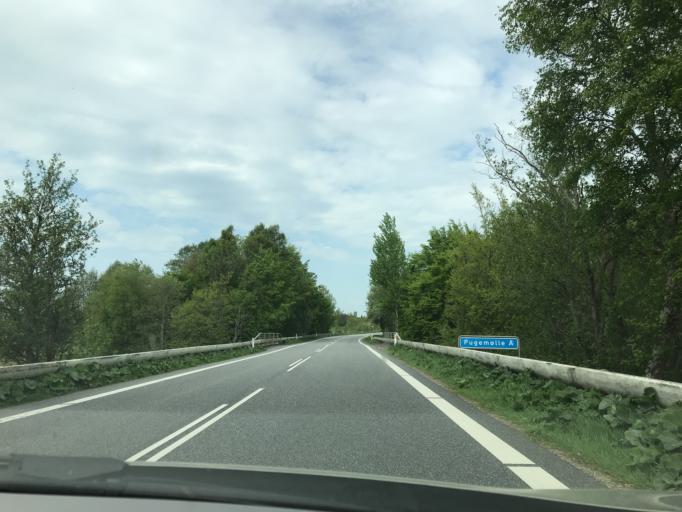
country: DK
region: South Denmark
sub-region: Assens Kommune
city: Assens
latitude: 55.3208
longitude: 9.9376
